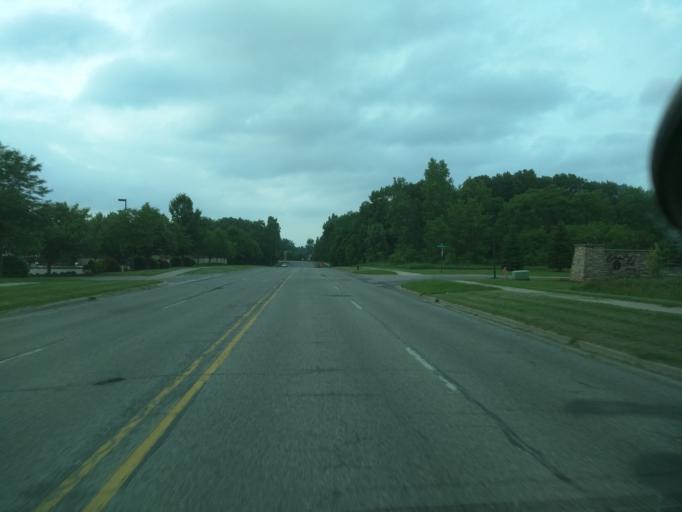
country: US
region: Michigan
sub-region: Ingham County
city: Okemos
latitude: 42.7235
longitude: -84.4102
